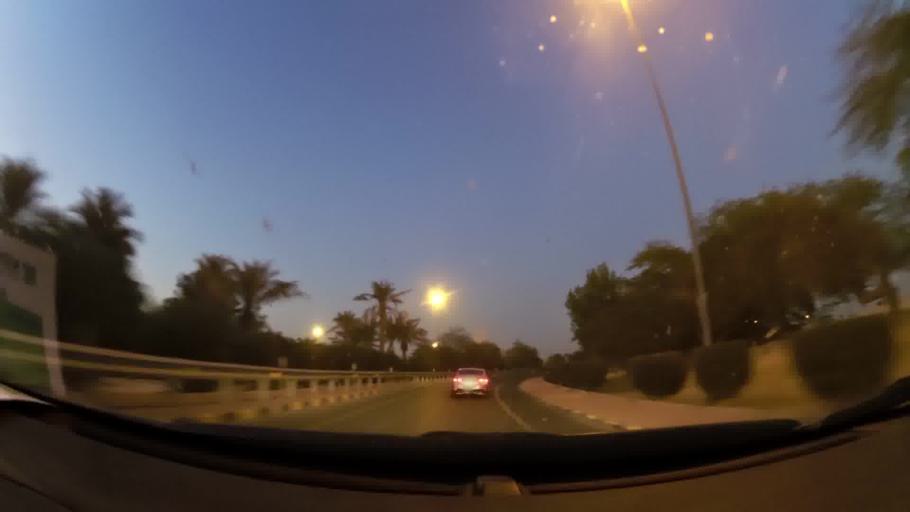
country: KW
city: Bayan
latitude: 29.3050
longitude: 48.0244
